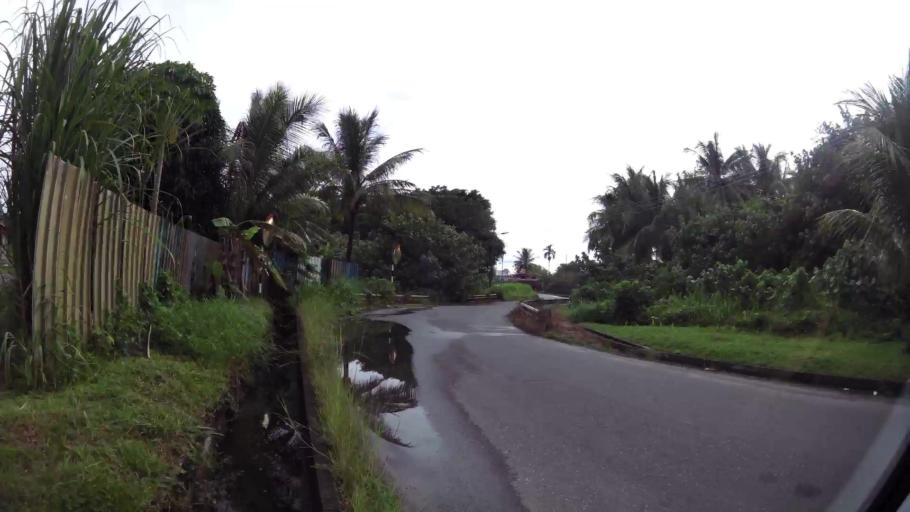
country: BN
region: Belait
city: Seria
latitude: 4.6143
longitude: 114.3587
